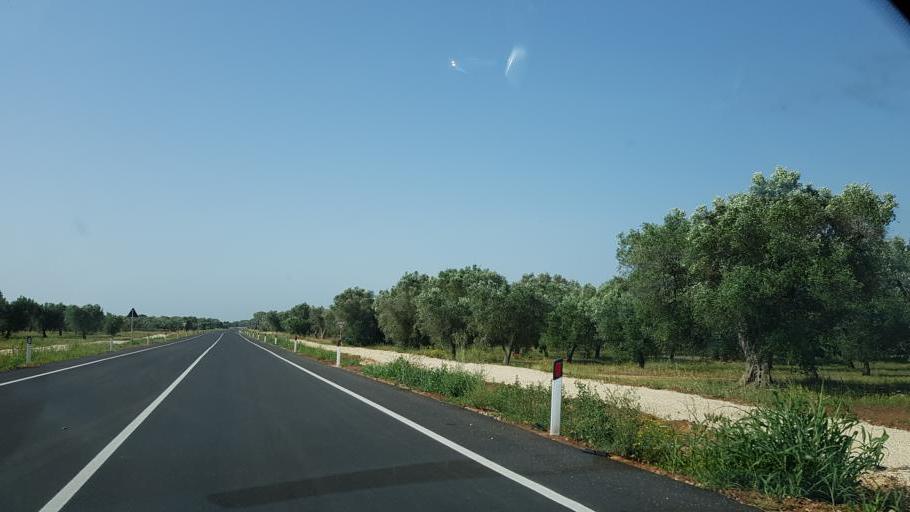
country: IT
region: Apulia
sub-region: Provincia di Brindisi
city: San Pancrazio Salentino
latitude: 40.4718
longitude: 17.8379
